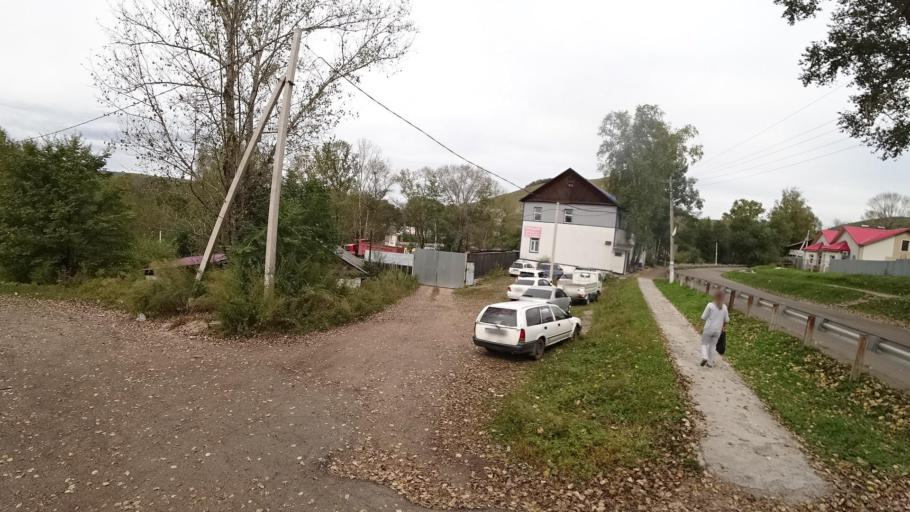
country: RU
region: Jewish Autonomous Oblast
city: Khingansk
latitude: 49.0173
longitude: 131.0601
